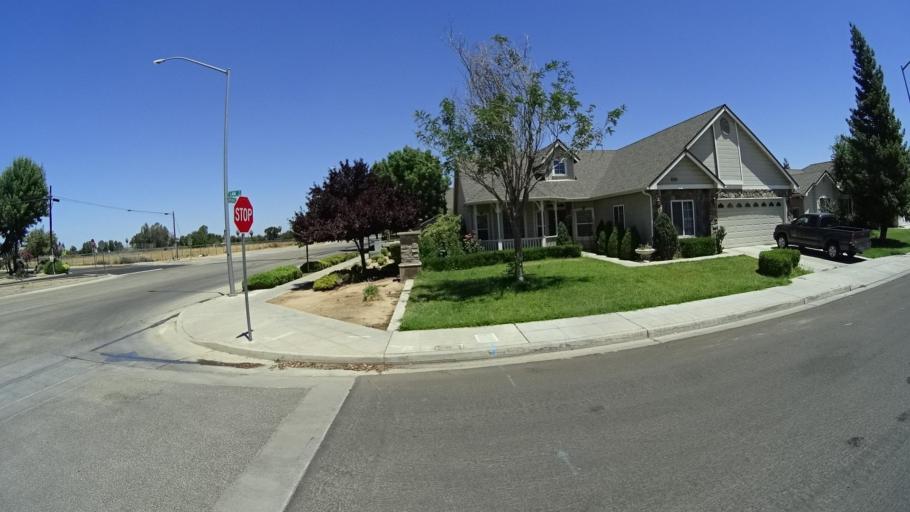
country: US
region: California
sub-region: Fresno County
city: Sunnyside
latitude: 36.7328
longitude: -119.6728
